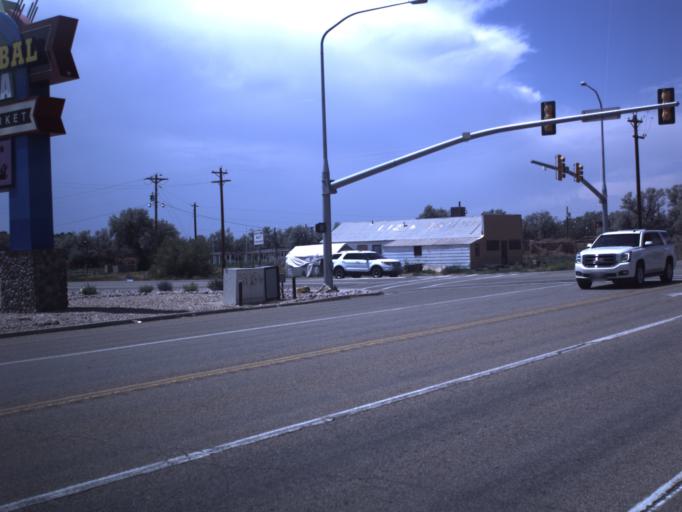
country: US
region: Utah
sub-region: Duchesne County
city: Roosevelt
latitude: 40.3019
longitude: -109.8587
